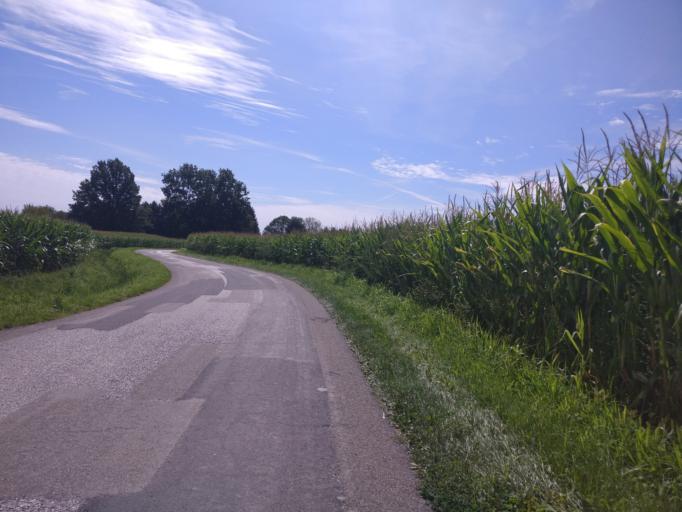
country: AT
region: Styria
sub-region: Politischer Bezirk Hartberg-Fuerstenfeld
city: Blaindorf
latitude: 47.1472
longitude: 15.8829
